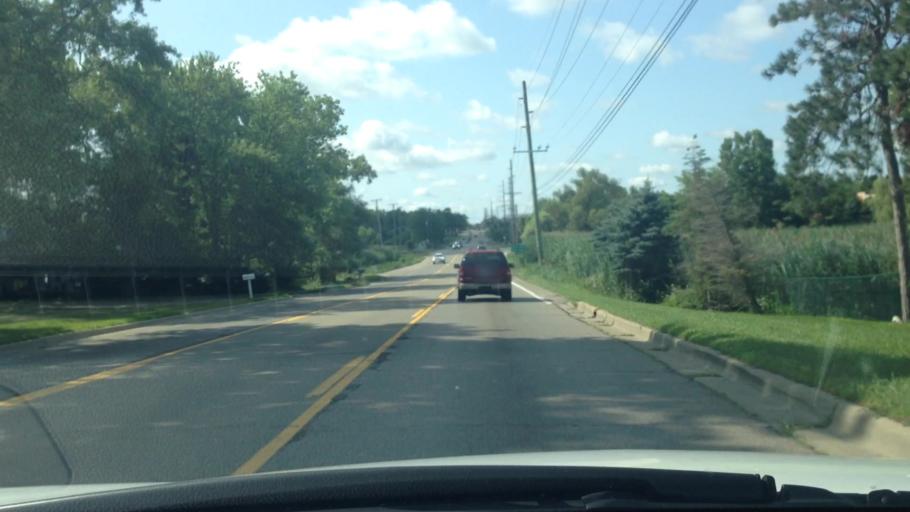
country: US
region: Michigan
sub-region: Oakland County
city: Wolverine Lake
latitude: 42.6051
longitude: -83.4466
